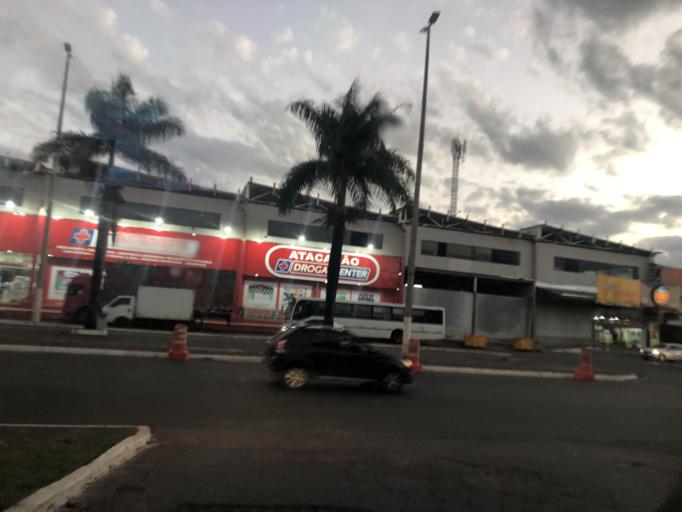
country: BR
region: Federal District
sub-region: Brasilia
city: Brasilia
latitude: -15.7949
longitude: -47.9464
